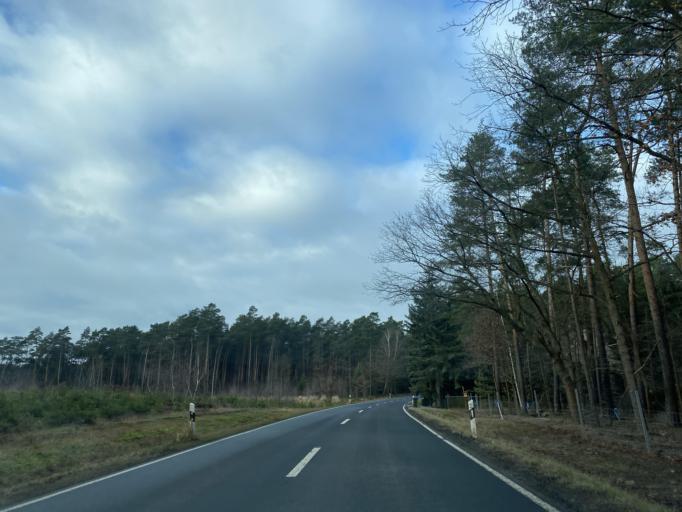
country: PL
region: Lubusz
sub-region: Powiat zarski
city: Leknica
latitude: 51.5024
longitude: 14.8060
